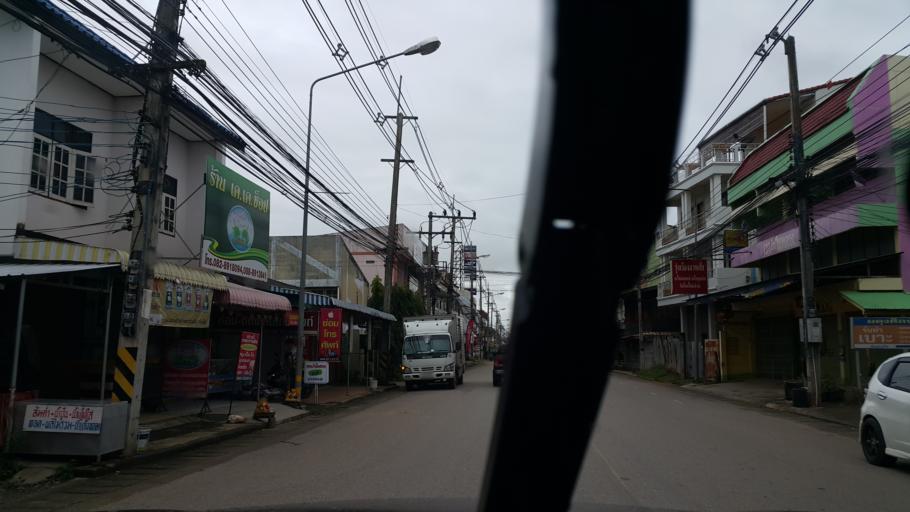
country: TH
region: Phayao
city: Chiang Kham
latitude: 19.5274
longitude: 100.3023
